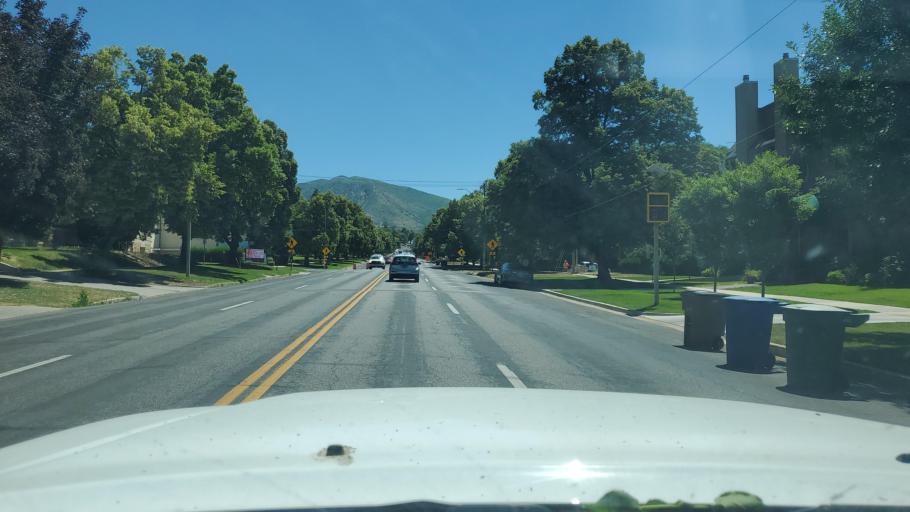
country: US
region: Utah
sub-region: Salt Lake County
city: Salt Lake City
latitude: 40.7672
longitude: -111.8636
